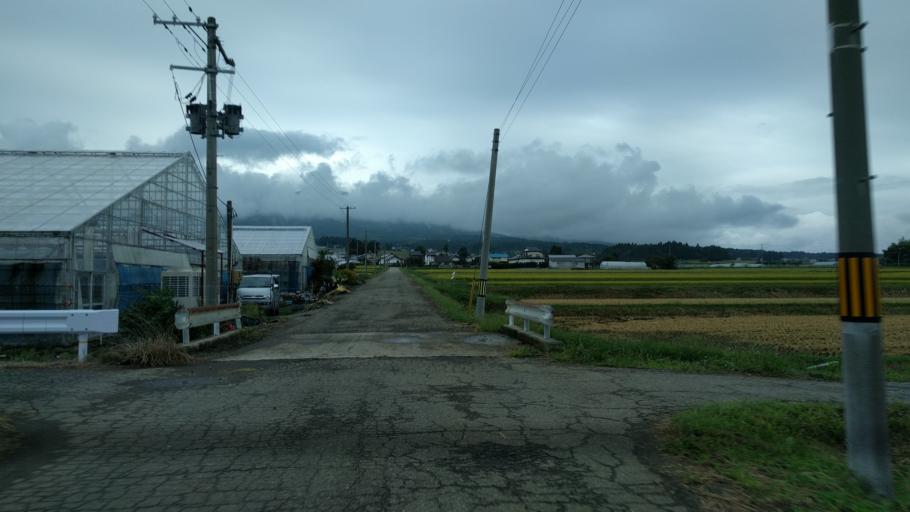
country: JP
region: Fukushima
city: Kitakata
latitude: 37.6240
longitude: 139.9157
